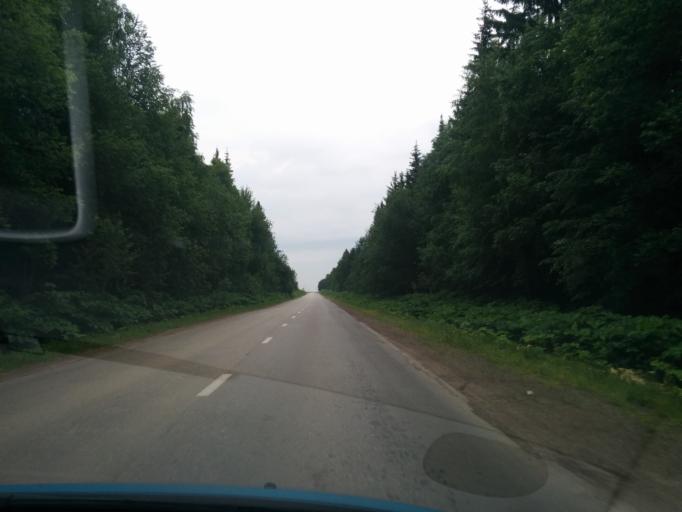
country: RU
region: Perm
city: Polazna
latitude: 58.2139
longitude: 56.2930
